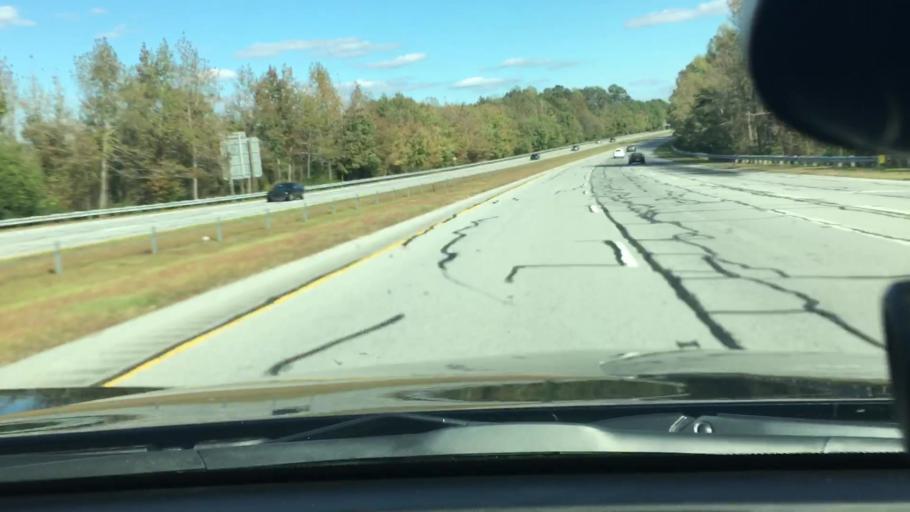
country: US
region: North Carolina
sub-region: Pitt County
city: Farmville
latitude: 35.6199
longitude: -77.6018
